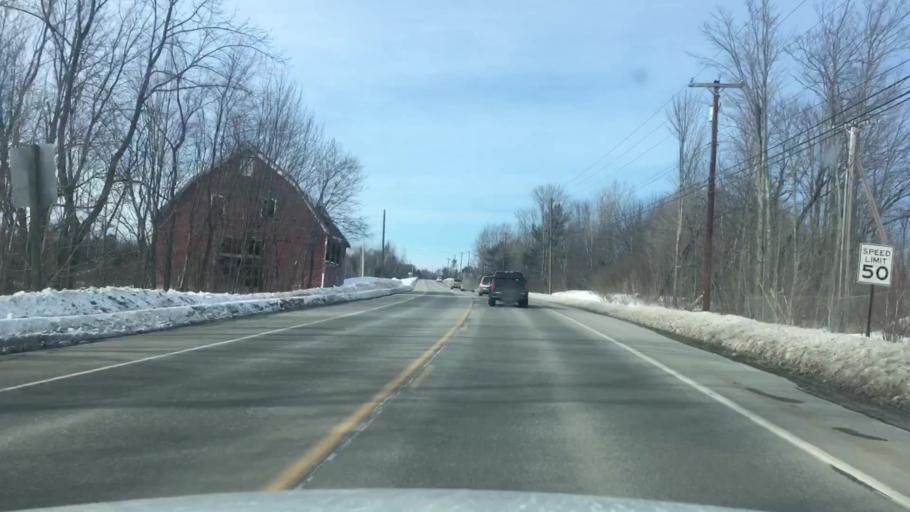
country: US
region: Maine
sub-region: Penobscot County
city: Kenduskeag
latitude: 44.9284
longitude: -68.9348
